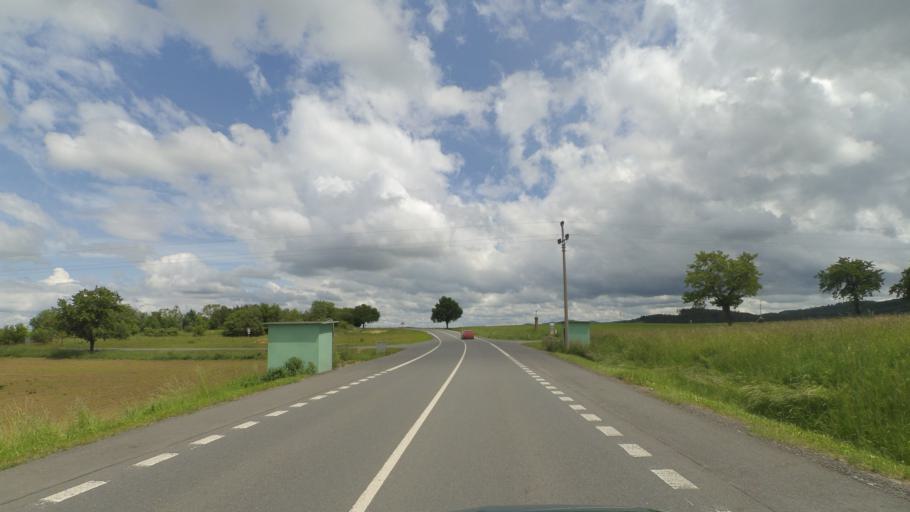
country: CZ
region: Plzensky
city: Janovice nad Uhlavou
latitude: 49.3658
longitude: 13.2438
